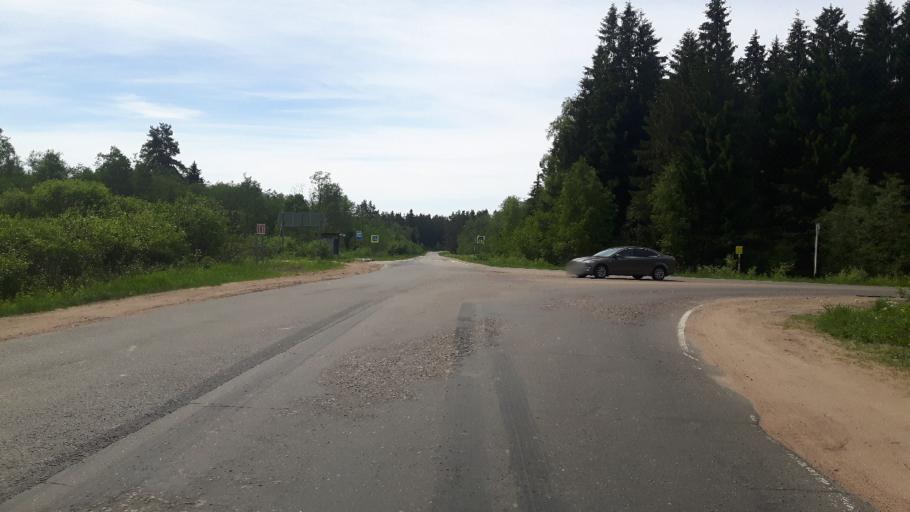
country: RU
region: Leningrad
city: Ust'-Luga
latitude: 59.6377
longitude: 28.2870
